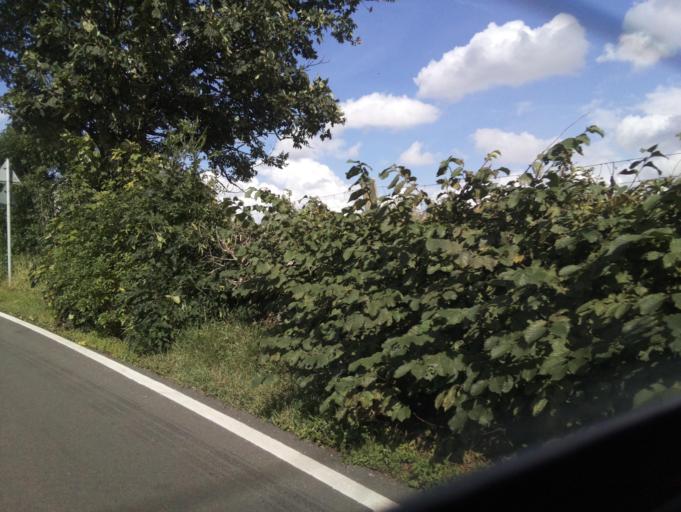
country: GB
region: England
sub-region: North Yorkshire
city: Leyburn
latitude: 54.3014
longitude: -1.8219
